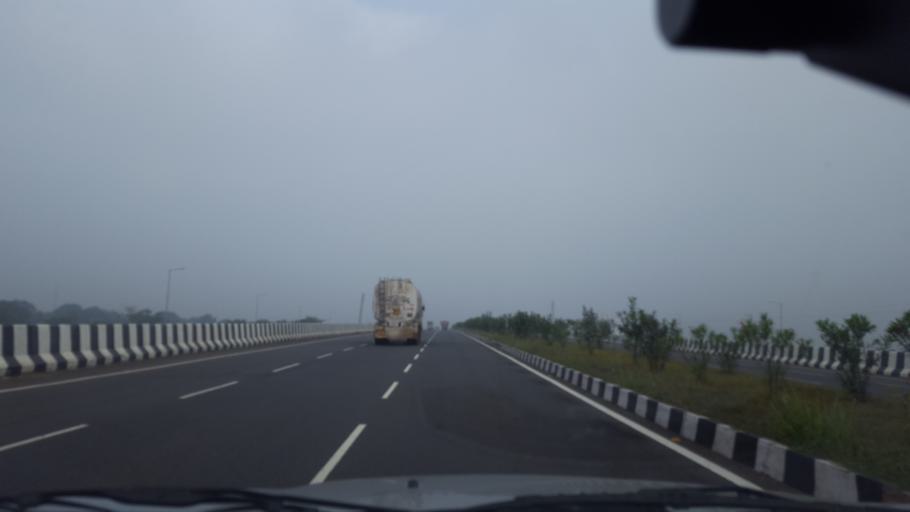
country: IN
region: Andhra Pradesh
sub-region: Prakasam
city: Ongole
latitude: 15.5306
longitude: 80.0544
